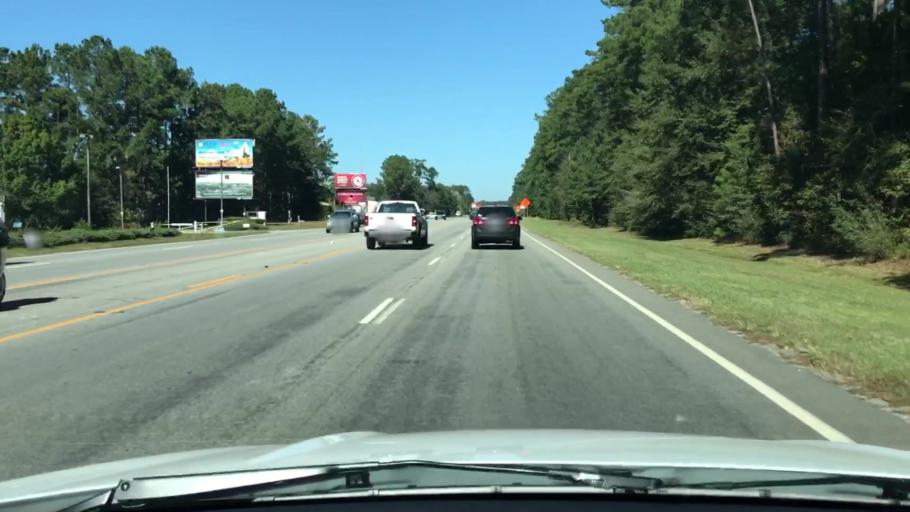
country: US
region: South Carolina
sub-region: Beaufort County
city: Bluffton
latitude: 32.3059
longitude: -80.9350
